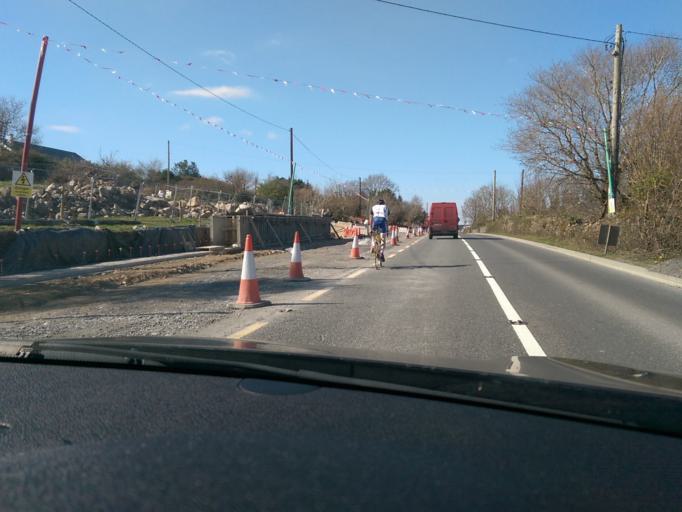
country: IE
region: Connaught
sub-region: County Galway
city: Moycullen
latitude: 53.3302
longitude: -9.1705
